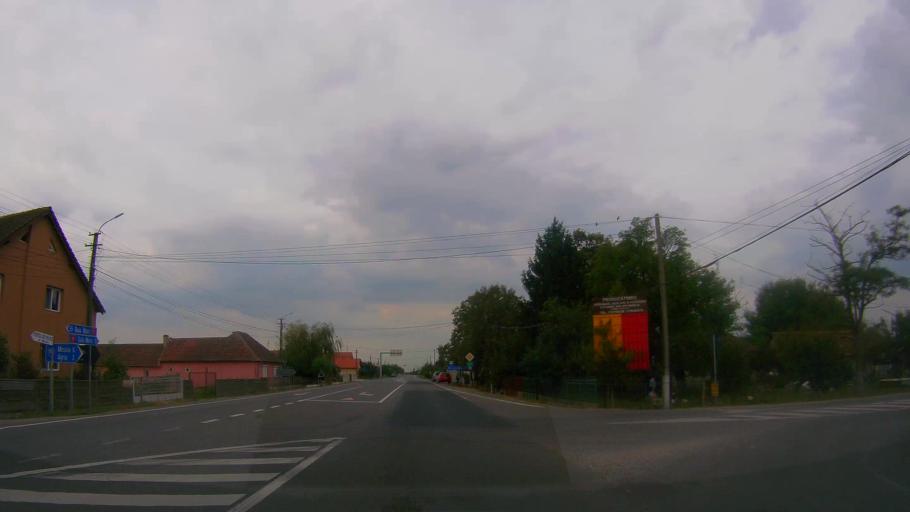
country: RO
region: Satu Mare
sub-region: Comuna Agris
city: Agris
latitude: 47.8656
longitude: 22.9989
